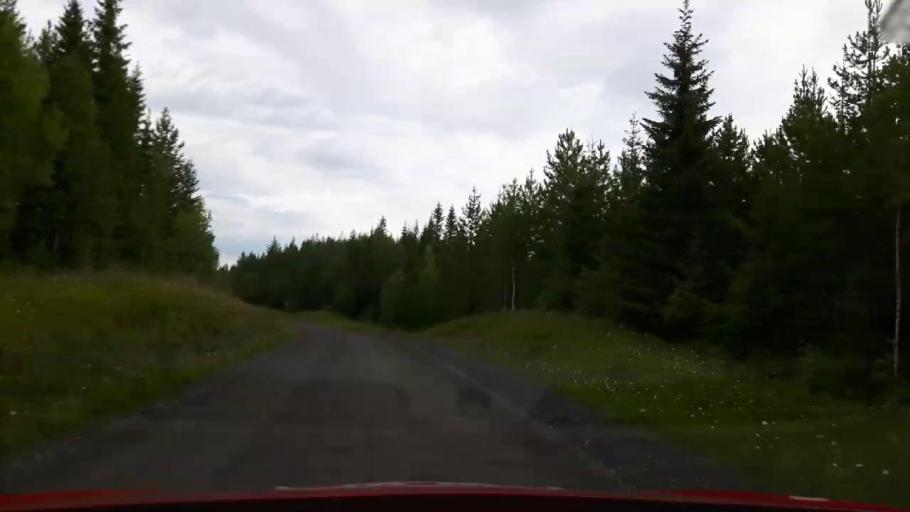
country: SE
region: Jaemtland
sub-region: OEstersunds Kommun
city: Lit
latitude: 63.4006
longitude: 15.2310
